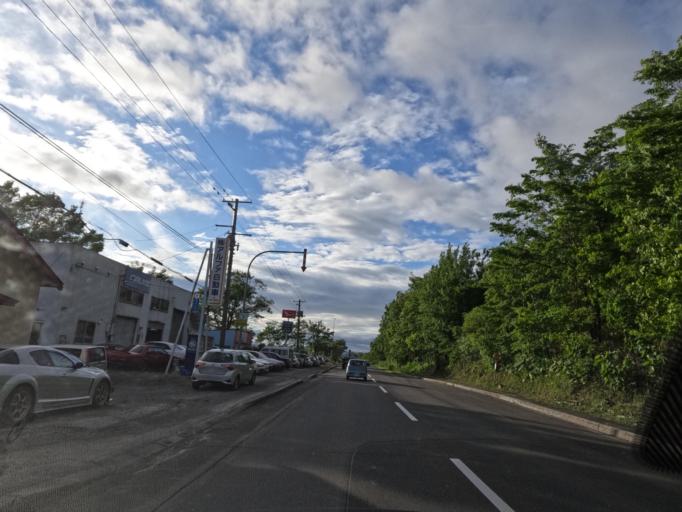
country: JP
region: Hokkaido
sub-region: Asahikawa-shi
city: Asahikawa
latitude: 43.7160
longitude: 142.3740
